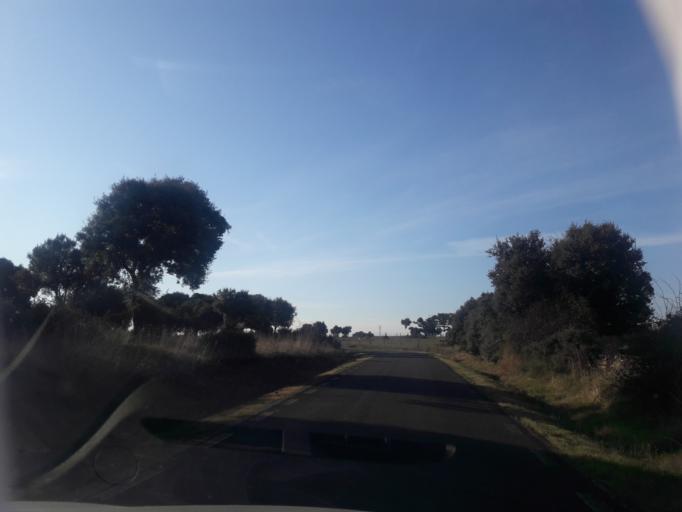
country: ES
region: Castille and Leon
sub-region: Provincia de Salamanca
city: Montejo
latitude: 40.6142
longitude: -5.6064
